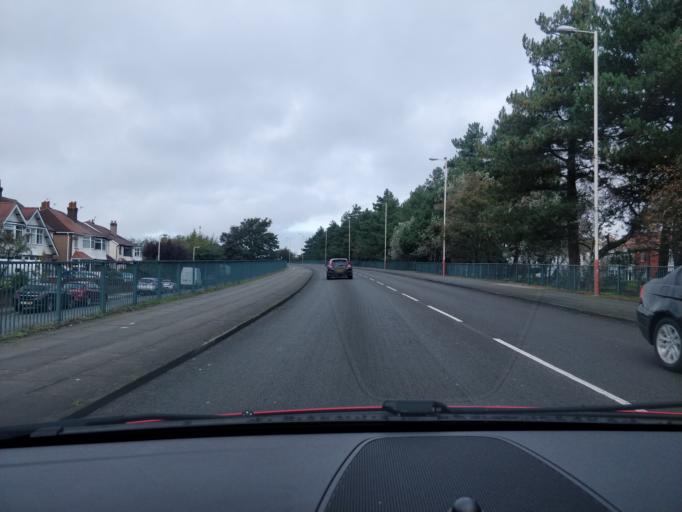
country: GB
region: England
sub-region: Sefton
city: Southport
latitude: 53.6205
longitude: -3.0233
